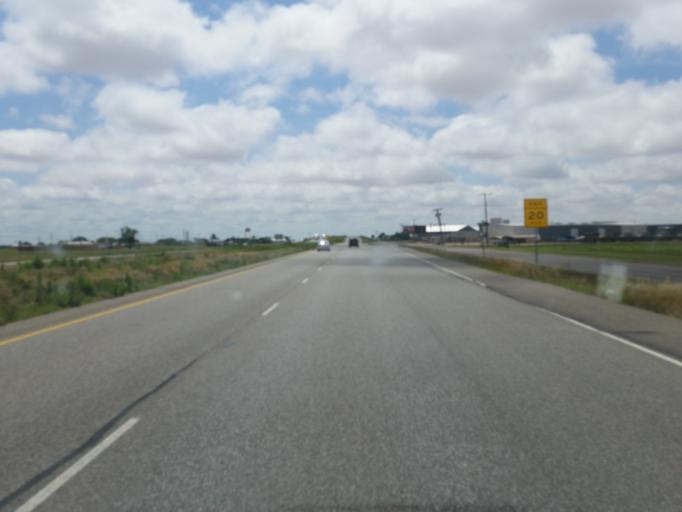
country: US
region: Texas
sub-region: Lubbock County
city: Slaton
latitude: 33.4235
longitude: -101.6492
